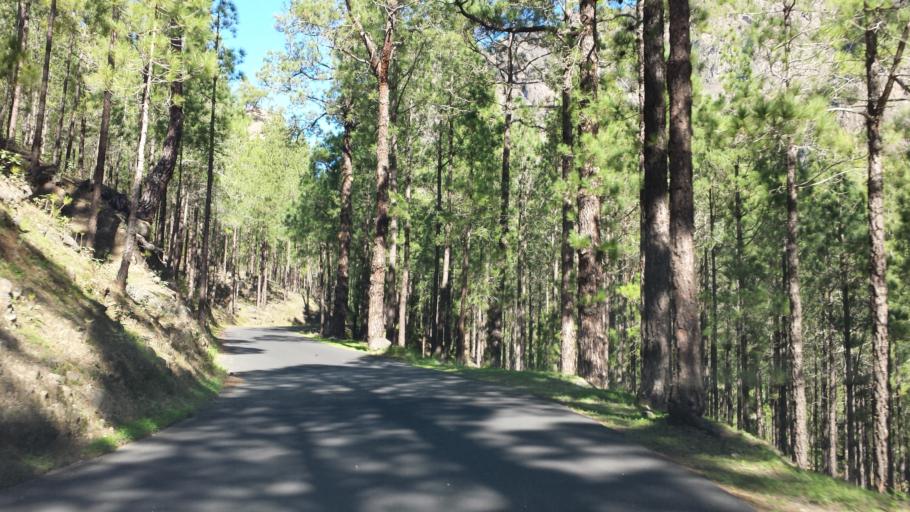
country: ES
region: Canary Islands
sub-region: Provincia de Santa Cruz de Tenerife
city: El Paso
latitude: 28.6837
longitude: -17.8482
